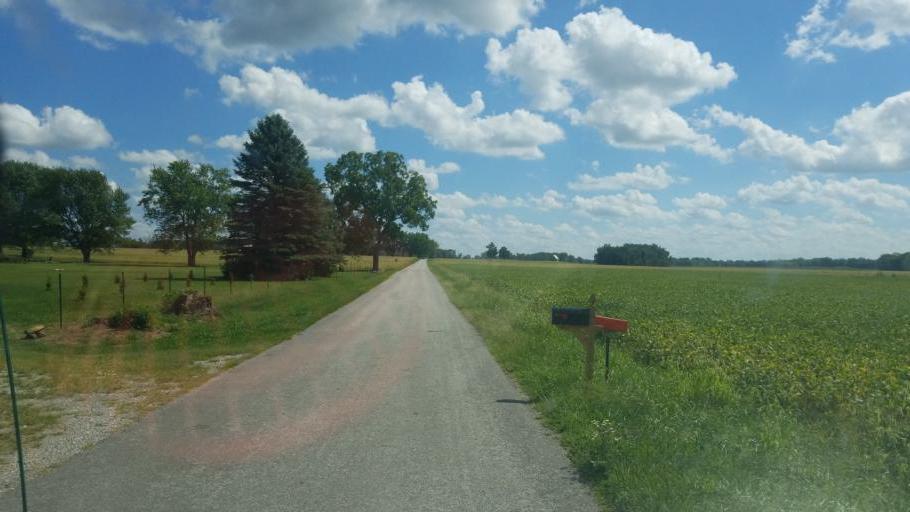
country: US
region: Ohio
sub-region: Marion County
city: Prospect
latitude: 40.4123
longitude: -83.1946
